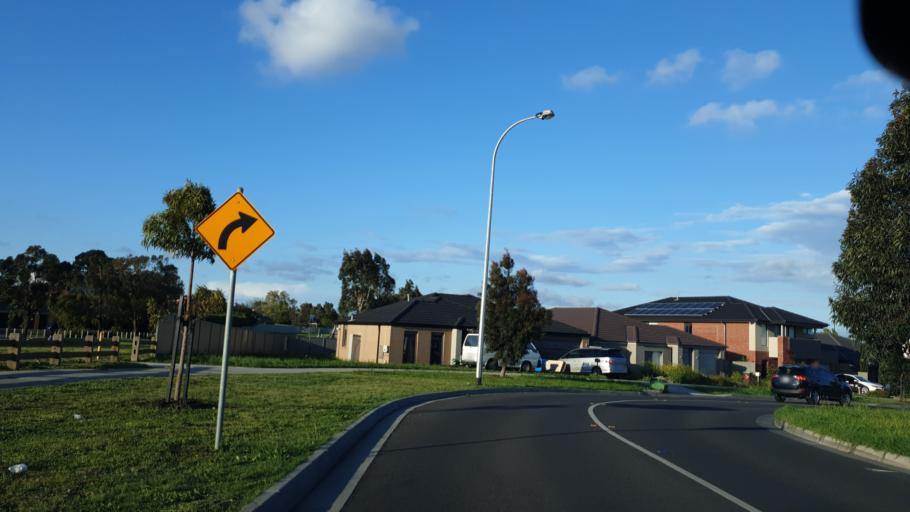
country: AU
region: Victoria
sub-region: Casey
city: Cranbourne East
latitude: -38.1087
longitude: 145.2976
